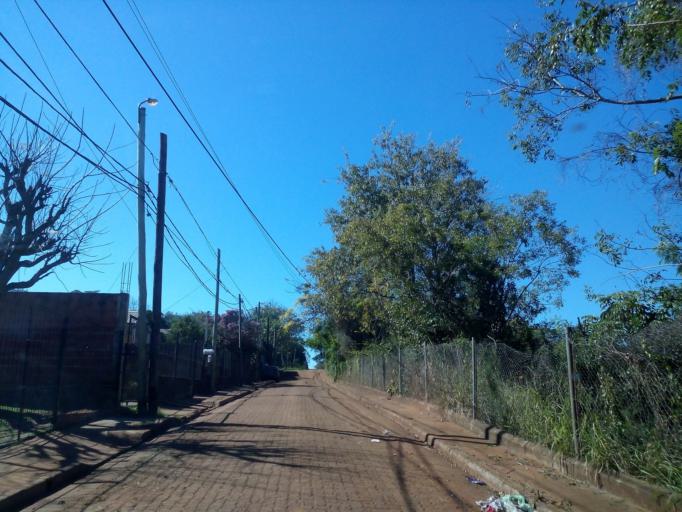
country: AR
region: Misiones
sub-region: Departamento de Capital
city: Posadas
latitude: -27.3900
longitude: -55.9399
